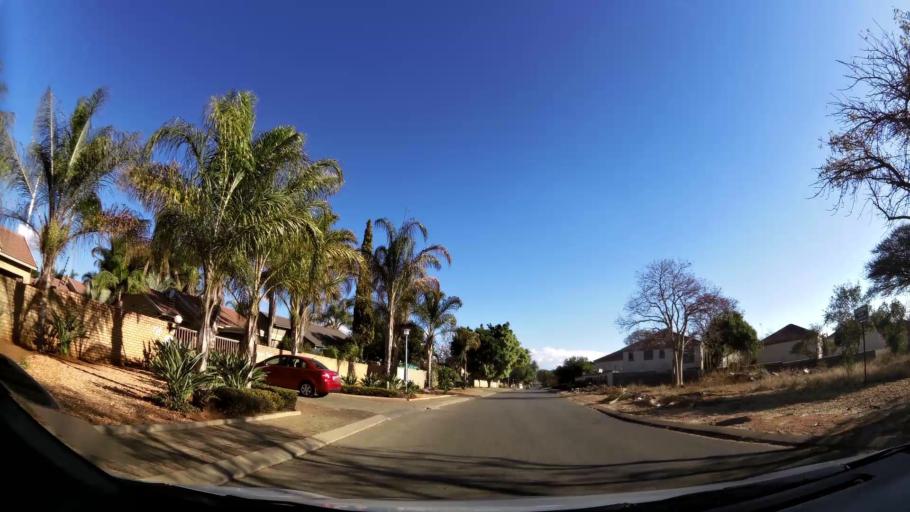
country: ZA
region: Limpopo
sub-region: Capricorn District Municipality
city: Polokwane
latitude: -23.8851
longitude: 29.4948
